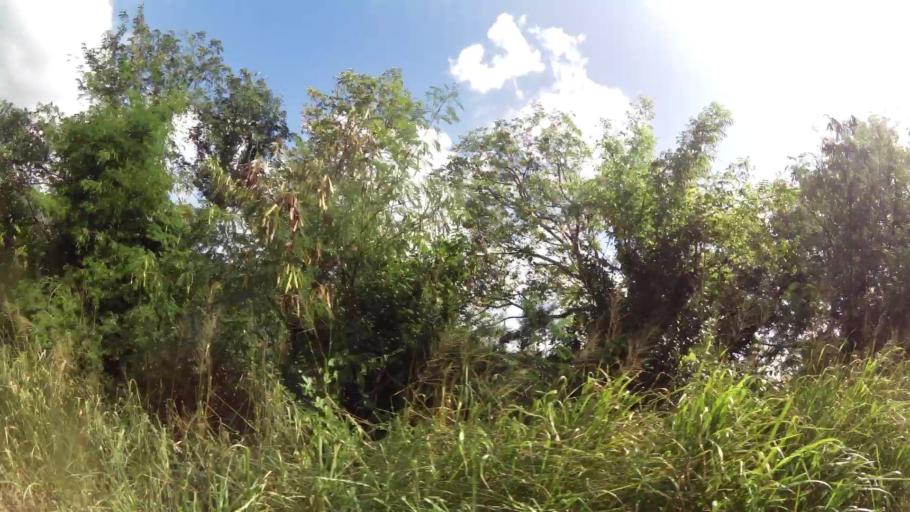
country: MQ
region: Martinique
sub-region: Martinique
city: Fort-de-France
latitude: 14.6370
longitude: -61.1329
